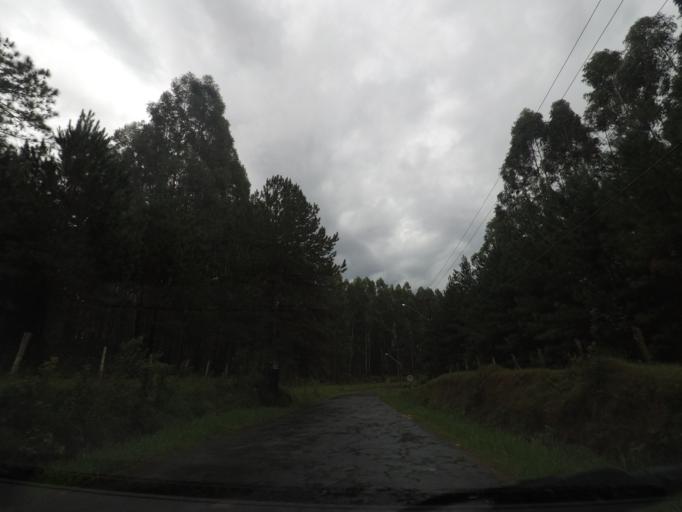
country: BR
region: Parana
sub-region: Campo Largo
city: Campo Largo
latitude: -25.4531
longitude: -49.4388
